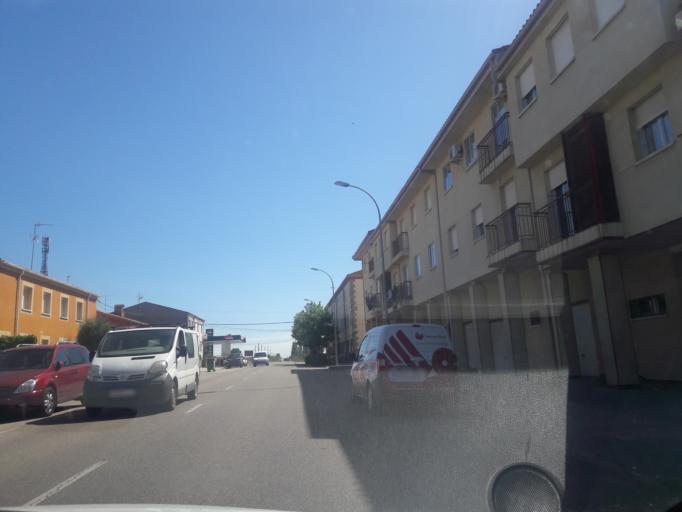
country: ES
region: Castille and Leon
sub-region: Provincia de Salamanca
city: Lumbrales
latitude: 40.9367
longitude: -6.7119
